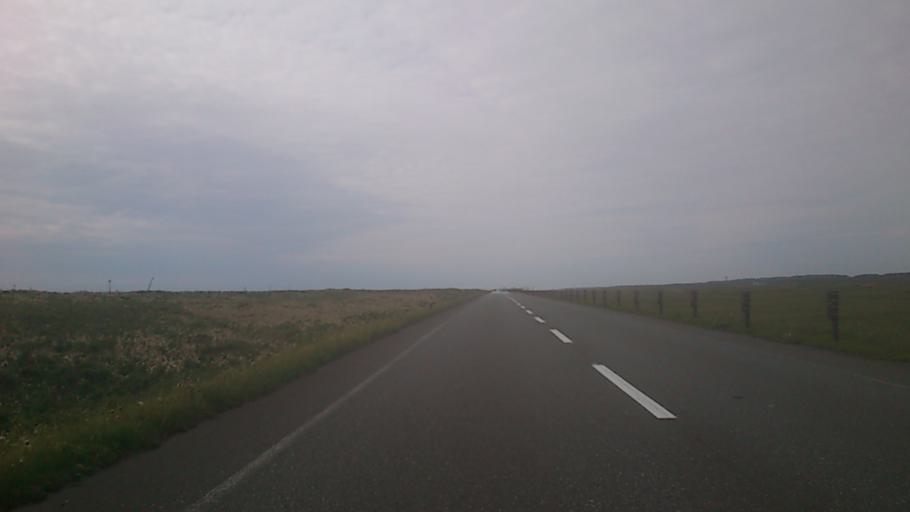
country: JP
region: Hokkaido
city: Wakkanai
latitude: 45.0649
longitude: 141.6443
